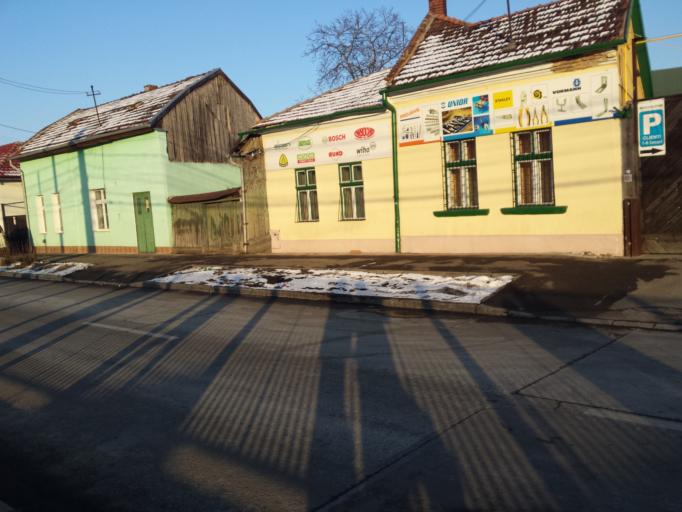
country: RO
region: Cluj
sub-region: Municipiul Cluj-Napoca
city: Cluj-Napoca
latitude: 46.7871
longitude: 23.5881
